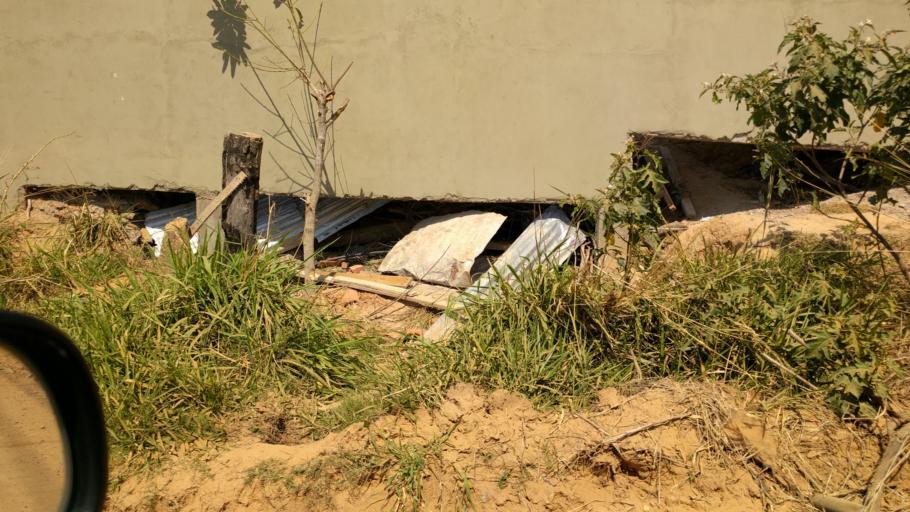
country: BO
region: Santa Cruz
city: Santa Cruz de la Sierra
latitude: -17.7588
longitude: -63.2290
